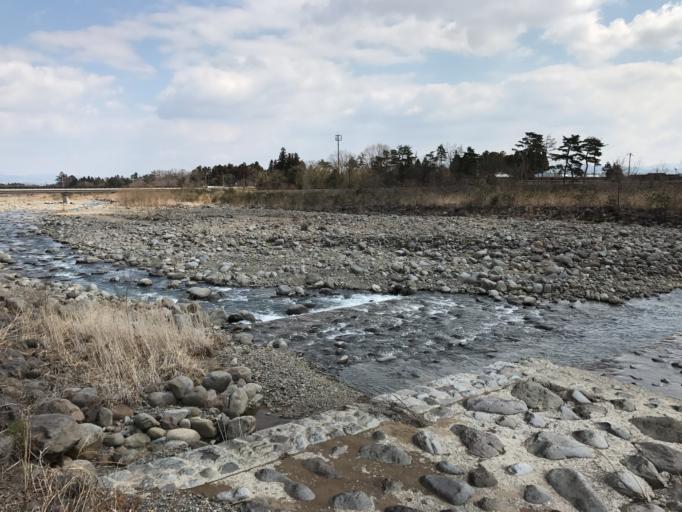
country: JP
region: Fukushima
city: Fukushima-shi
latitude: 37.7250
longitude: 140.3700
